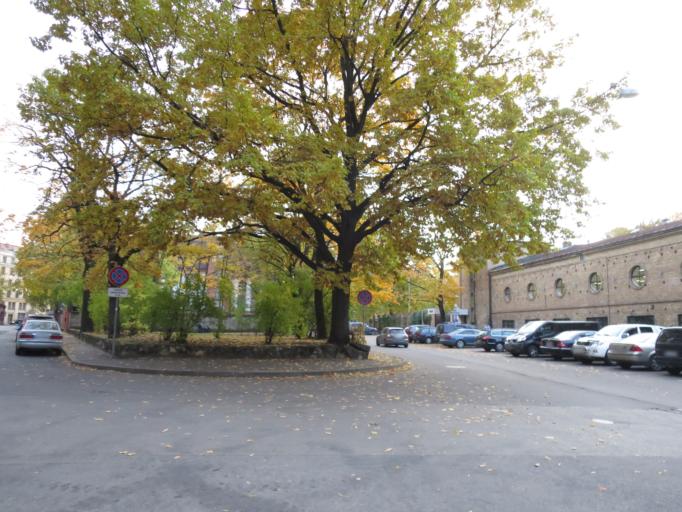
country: LV
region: Riga
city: Riga
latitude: 56.9620
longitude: 24.1282
